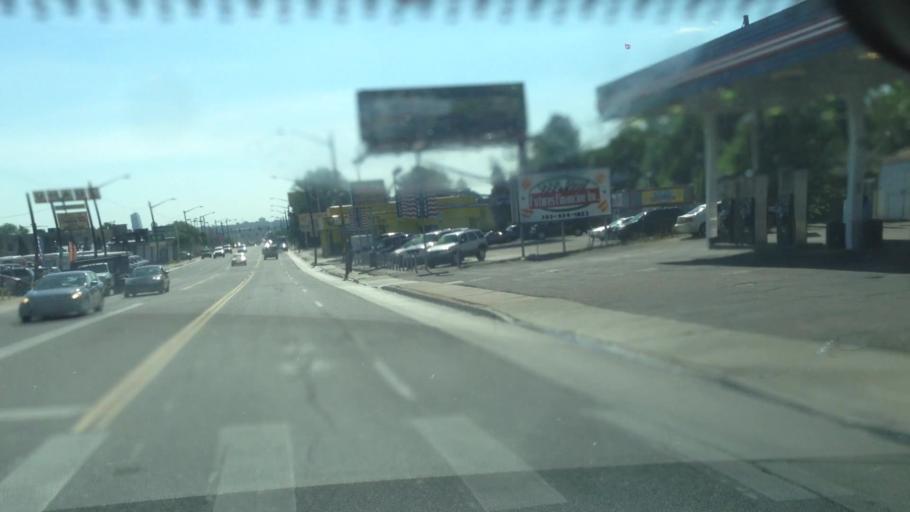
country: US
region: Colorado
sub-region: Denver County
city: Denver
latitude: 39.7111
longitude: -105.0204
